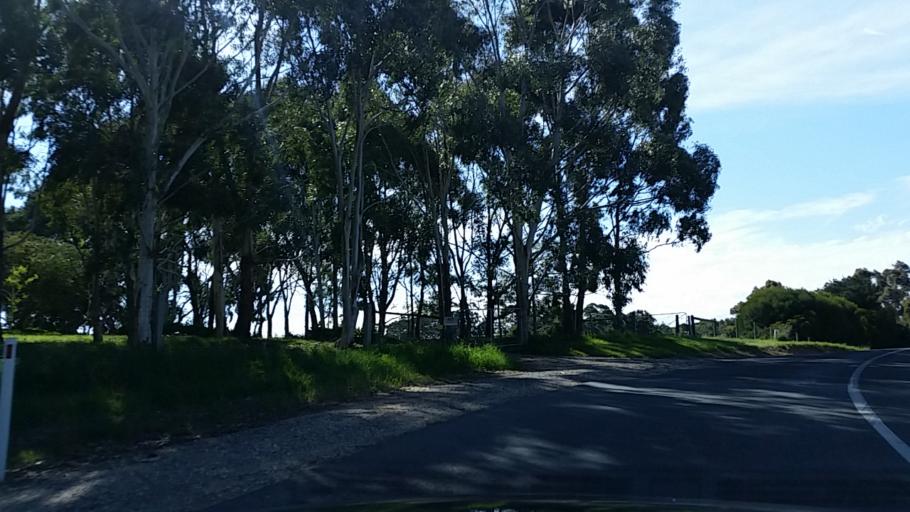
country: AU
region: South Australia
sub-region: Mount Barker
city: Little Hampton
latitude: -35.0796
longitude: 138.8198
